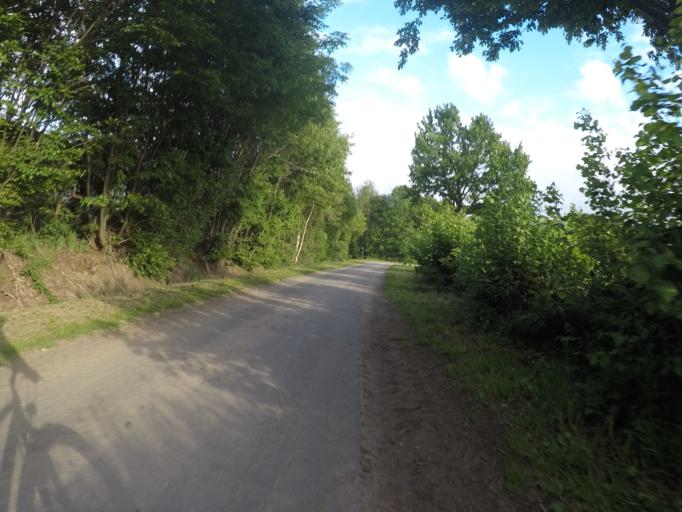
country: DE
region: Schleswig-Holstein
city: Bonningstedt
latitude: 53.6860
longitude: 9.9271
